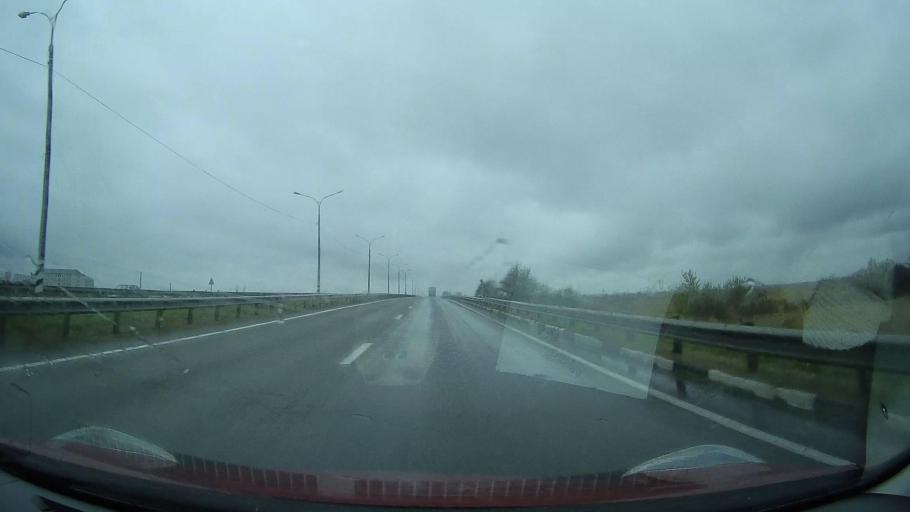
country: RU
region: Stavropol'skiy
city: Nevinnomyssk
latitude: 44.6364
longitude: 41.9954
